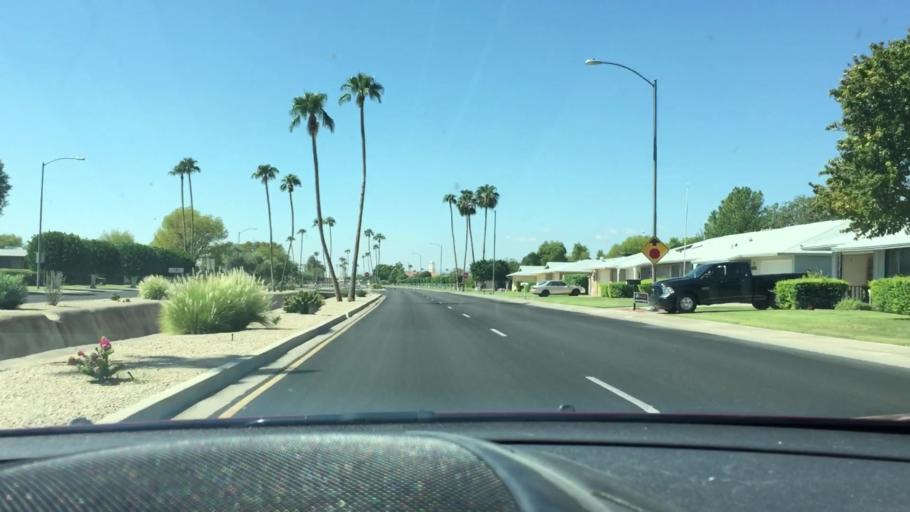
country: US
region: Arizona
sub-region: Maricopa County
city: Sun City
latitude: 33.6446
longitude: -112.2817
